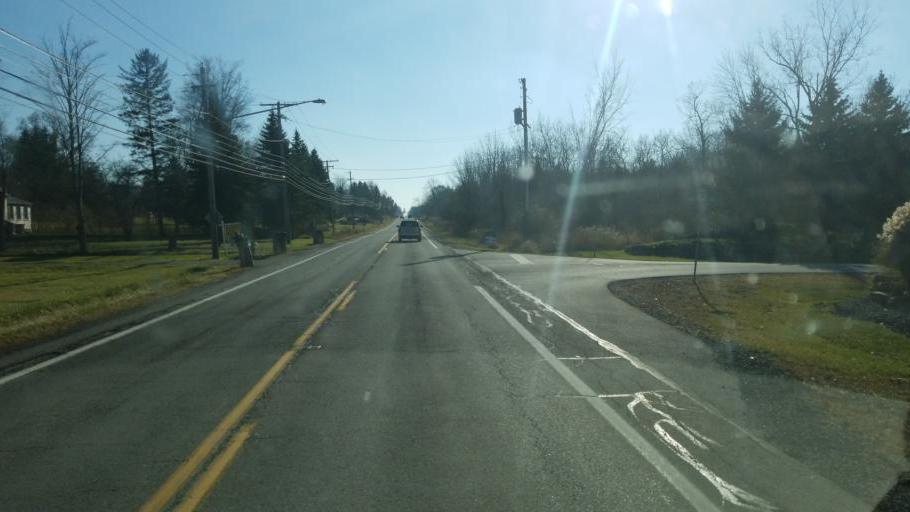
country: US
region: Ohio
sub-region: Geauga County
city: Burton
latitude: 41.5238
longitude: -81.1939
